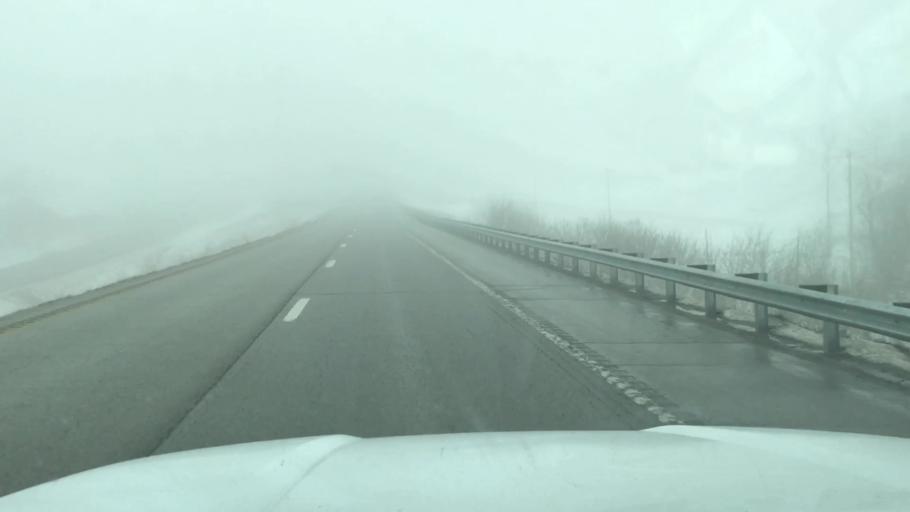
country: US
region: Missouri
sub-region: Clinton County
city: Cameron
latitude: 39.7548
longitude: -94.2945
